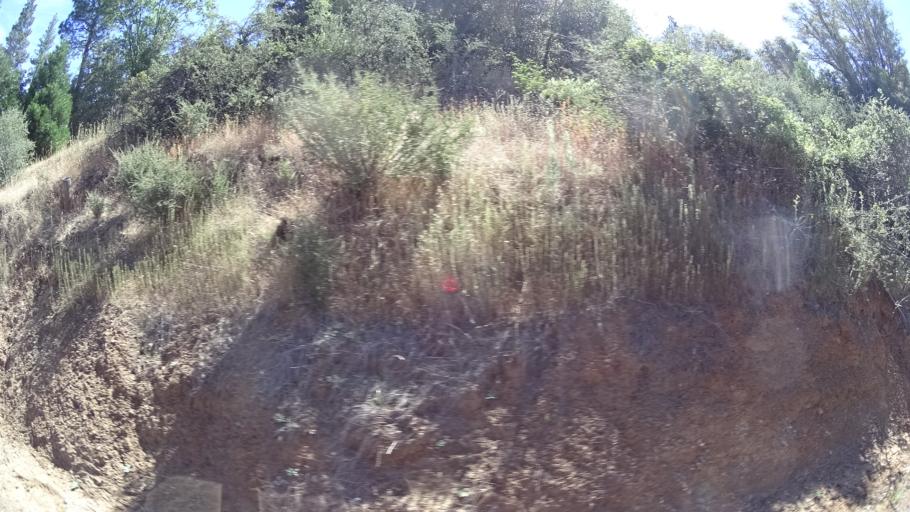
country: US
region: California
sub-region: Amador County
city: Pioneer
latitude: 38.3452
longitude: -120.5817
